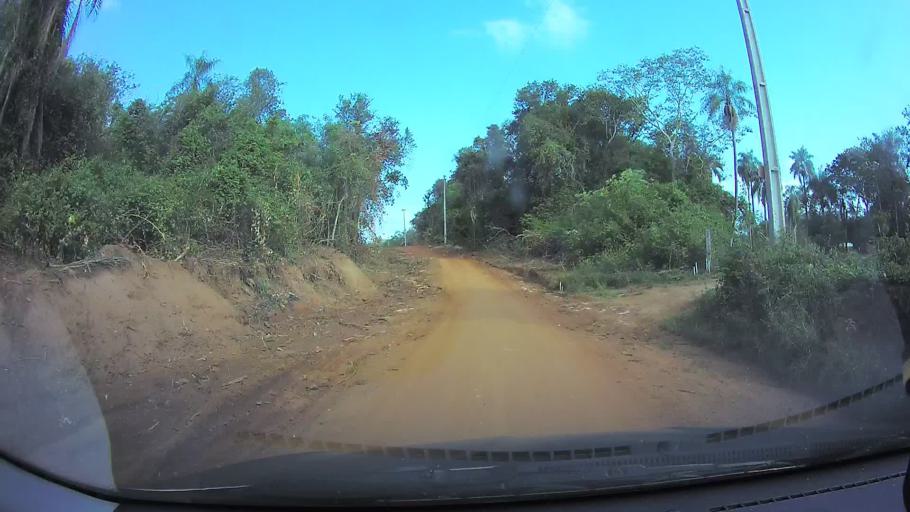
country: PY
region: Cordillera
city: Arroyos y Esteros
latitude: -25.0131
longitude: -57.1983
